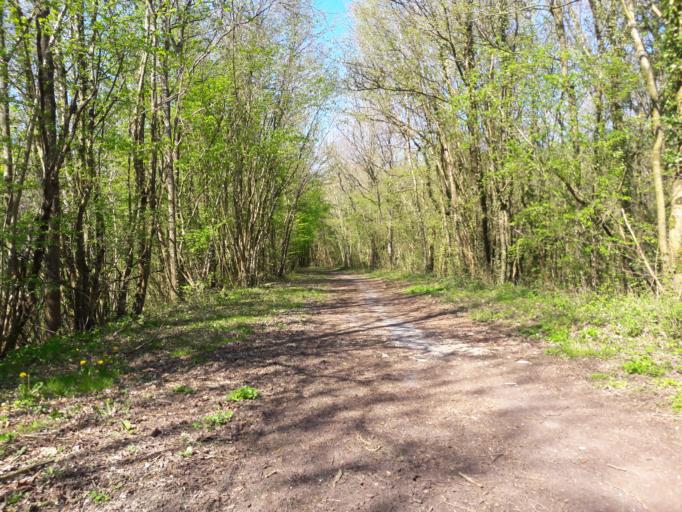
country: FR
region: Nord-Pas-de-Calais
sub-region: Departement du Nord
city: Sains-du-Nord
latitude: 50.1238
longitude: 4.0676
